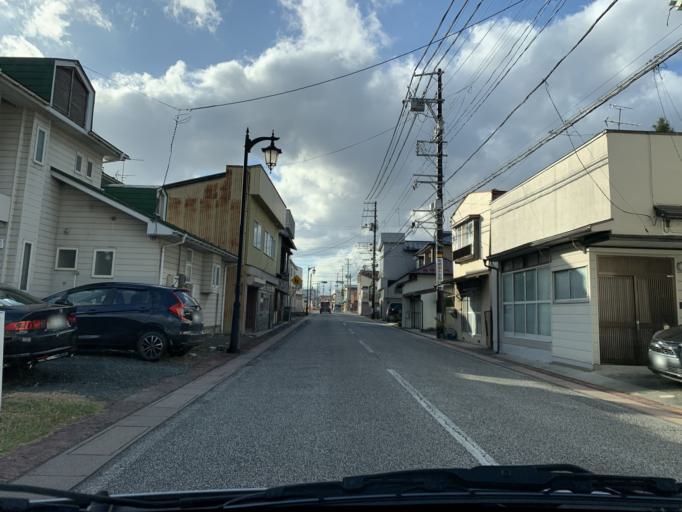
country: JP
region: Iwate
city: Mizusawa
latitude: 39.1440
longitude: 141.1348
